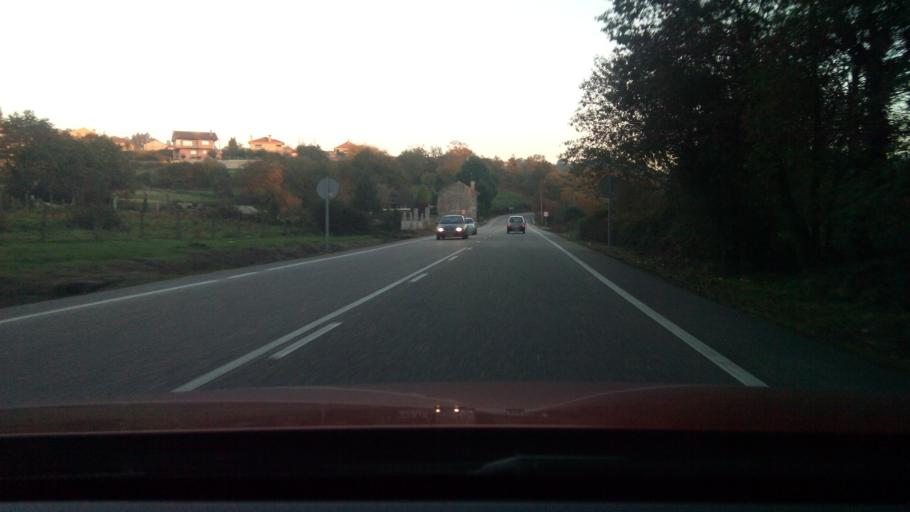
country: ES
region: Galicia
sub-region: Provincia de Pontevedra
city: Gondomar
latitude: 42.1620
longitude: -8.6974
